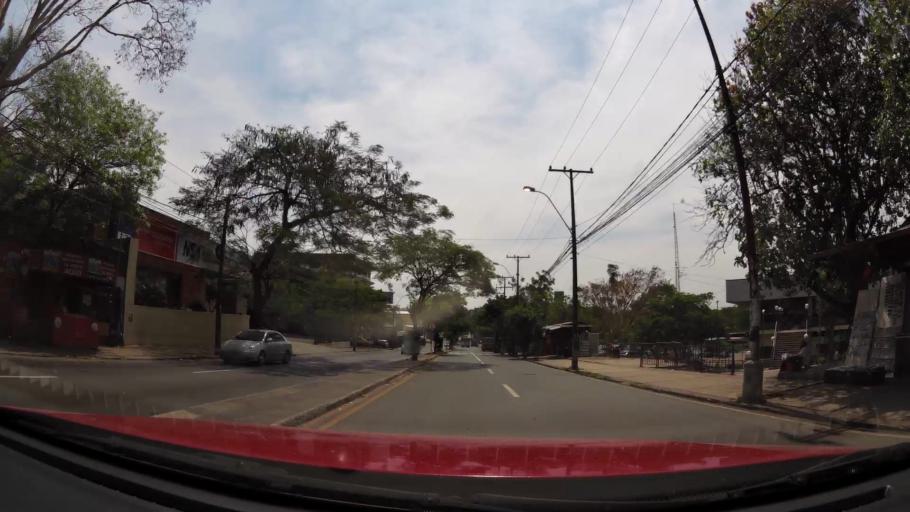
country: PY
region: Central
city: Lambare
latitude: -25.3255
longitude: -57.5970
